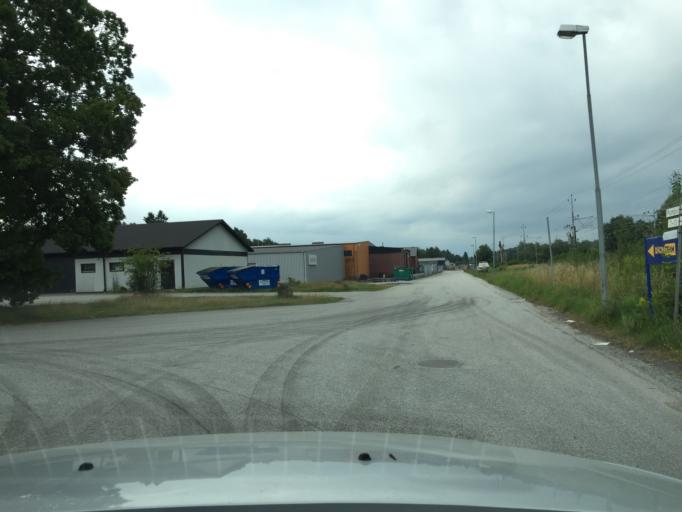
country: SE
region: Skane
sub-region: Hoors Kommun
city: Hoeoer
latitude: 55.9525
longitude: 13.5600
